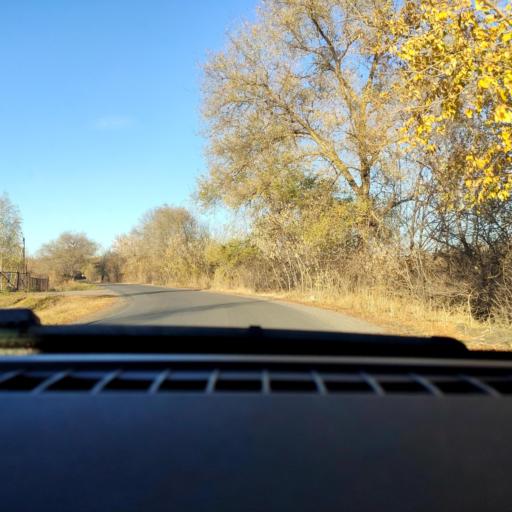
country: RU
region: Voronezj
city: Novaya Usman'
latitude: 51.6394
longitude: 39.3065
